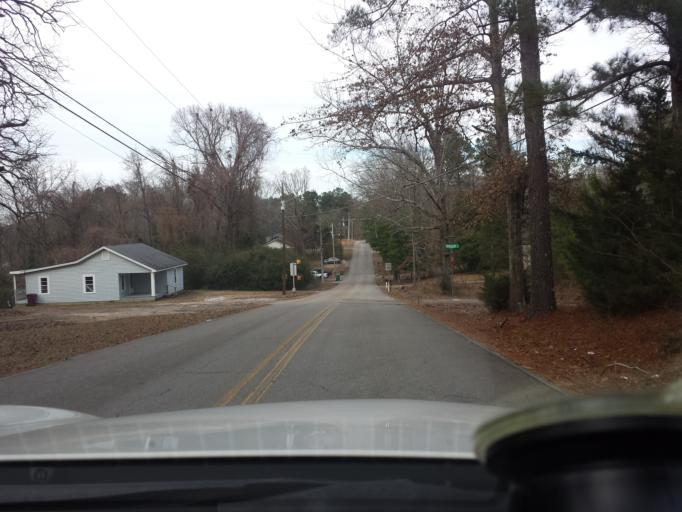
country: US
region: Mississippi
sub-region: Lee County
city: Tupelo
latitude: 34.2621
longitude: -88.6672
